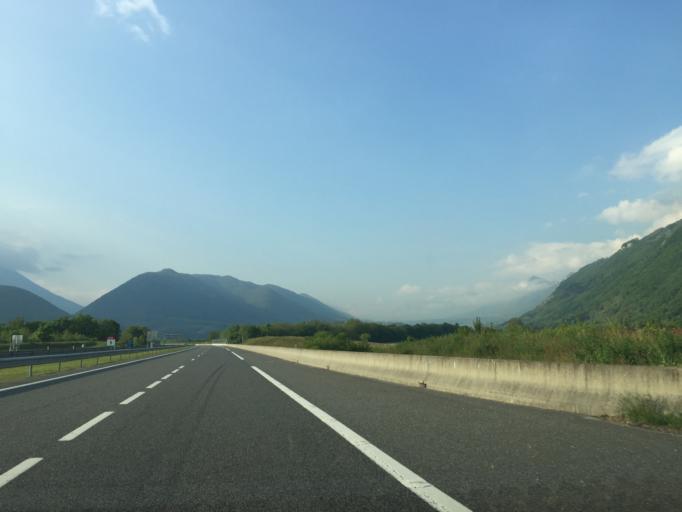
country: FR
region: Rhone-Alpes
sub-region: Departement de l'Isere
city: Vif
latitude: 45.0765
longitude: 5.6795
